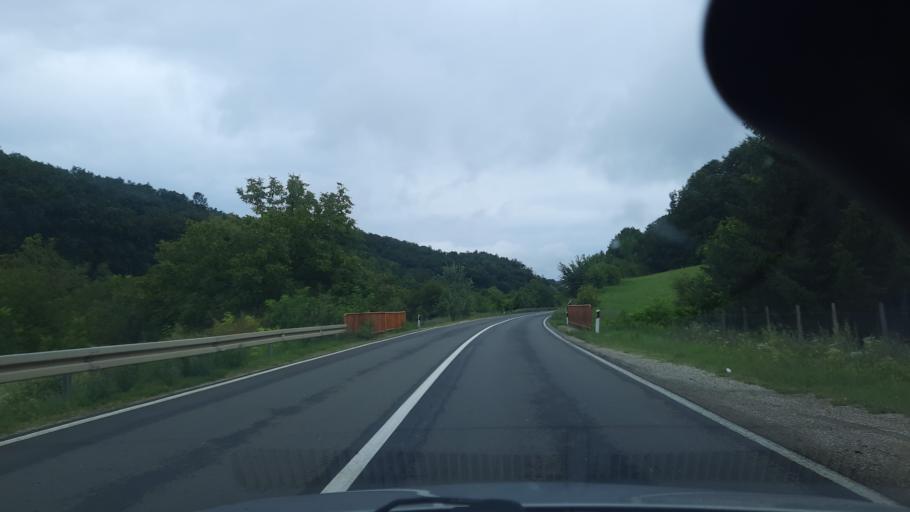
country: RS
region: Central Serbia
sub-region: Sumadijski Okrug
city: Knic
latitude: 43.9623
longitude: 20.8098
